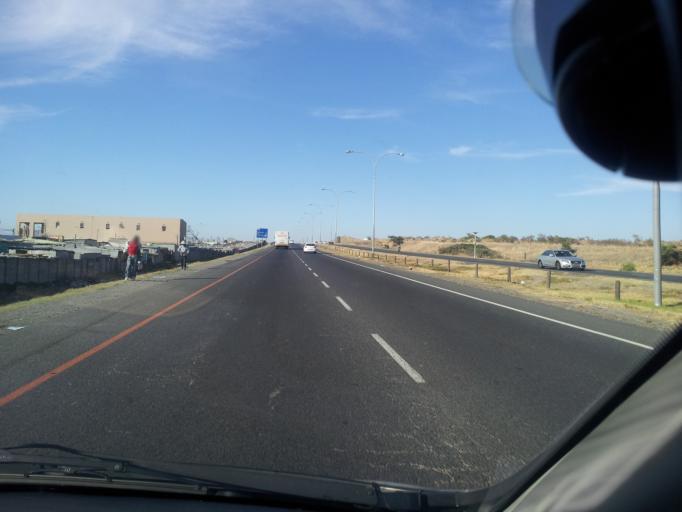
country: ZA
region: Western Cape
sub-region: City of Cape Town
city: Sunset Beach
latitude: -33.8266
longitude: 18.5409
